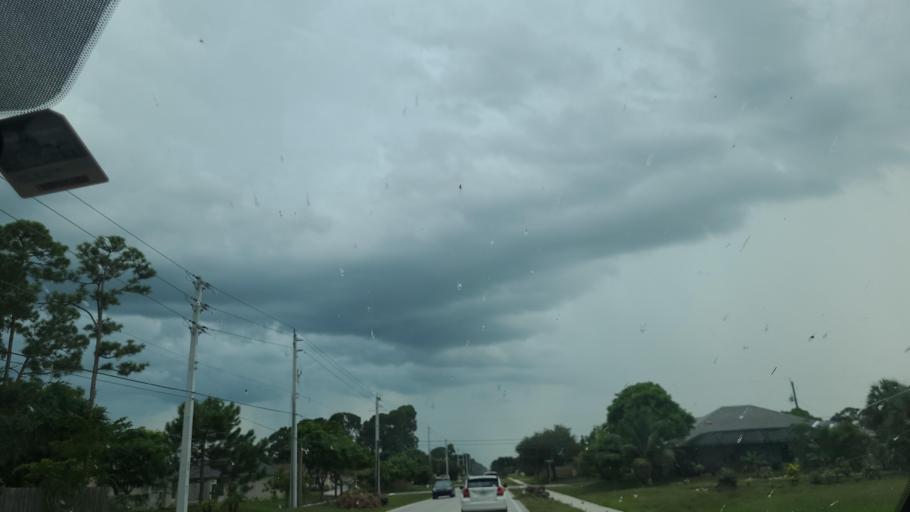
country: US
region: Florida
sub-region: Saint Lucie County
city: Port Saint Lucie
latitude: 27.2406
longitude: -80.3997
